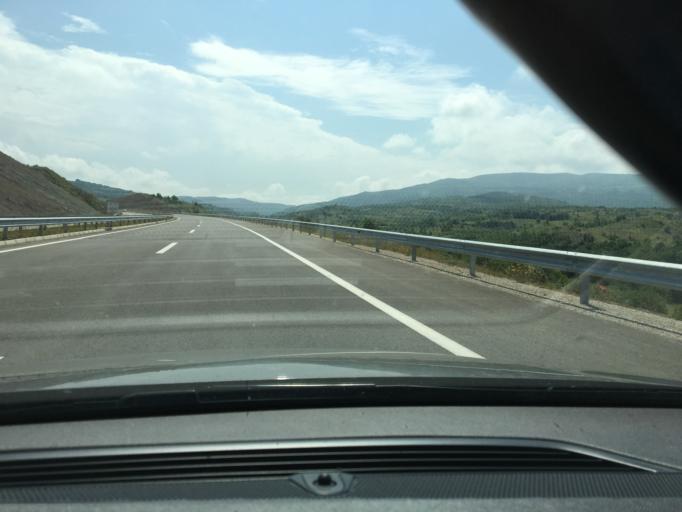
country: MK
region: Petrovec
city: Sredno Konjare
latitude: 41.9556
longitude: 21.7351
